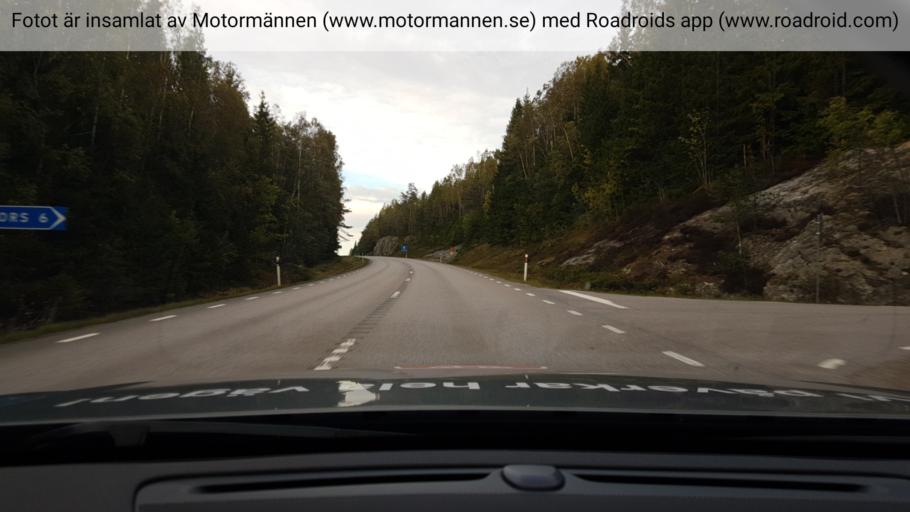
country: SE
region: Vaestra Goetaland
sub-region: Bengtsfors Kommun
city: Dals Langed
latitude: 59.0306
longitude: 12.4171
